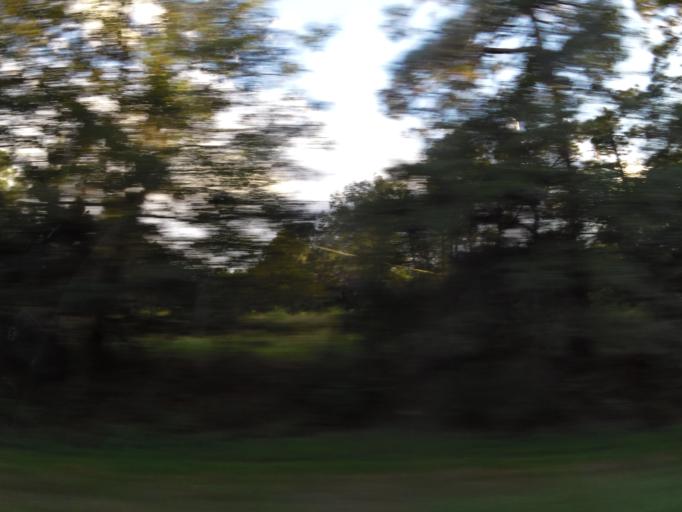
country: US
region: Georgia
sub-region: Lowndes County
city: Valdosta
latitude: 30.7857
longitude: -83.1687
